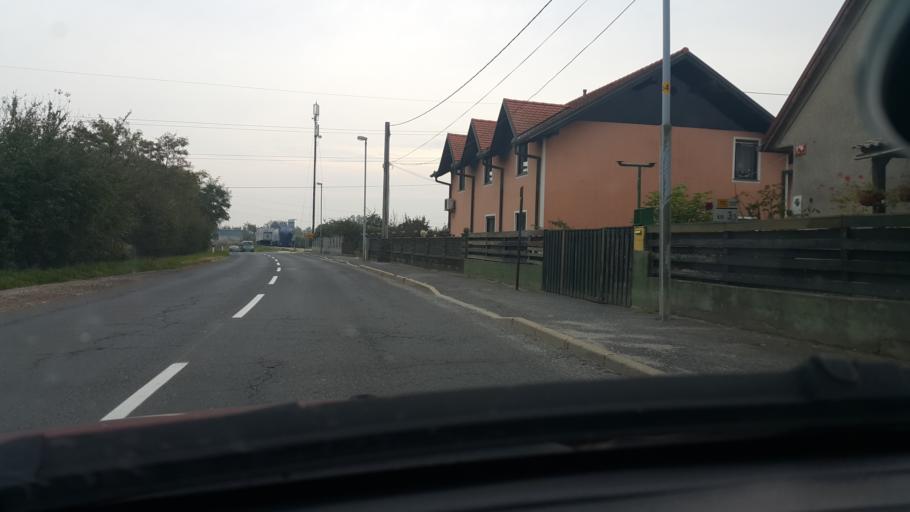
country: SI
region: Miklavz na Dravskem Polju
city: Miklavz na Dravskem Polju
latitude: 46.5303
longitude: 15.6959
